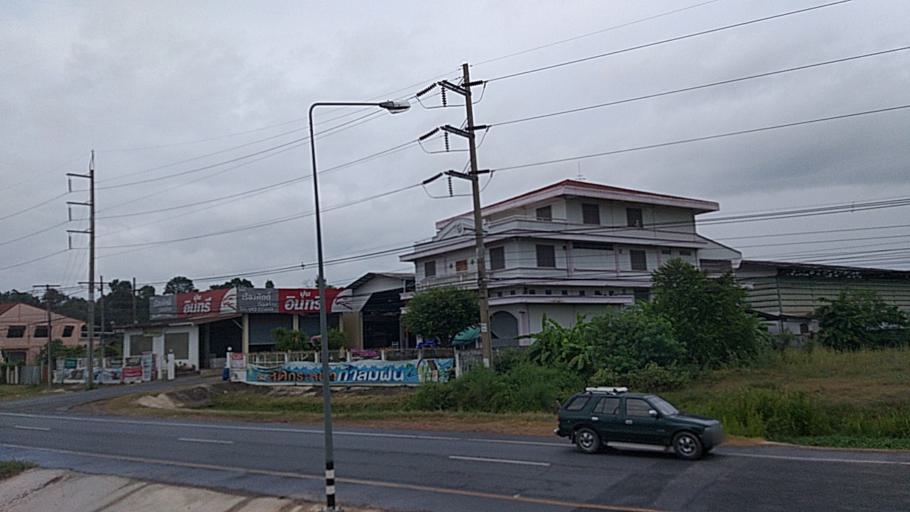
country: TH
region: Maha Sarakham
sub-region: Amphoe Borabue
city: Borabue
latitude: 16.0489
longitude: 103.1272
